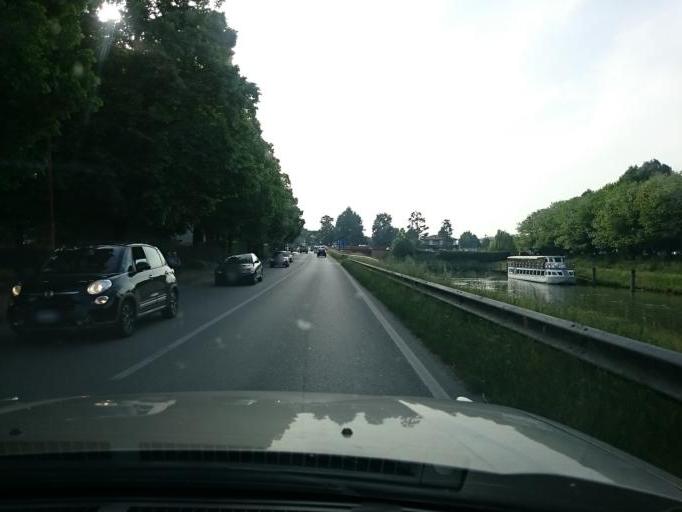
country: IT
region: Veneto
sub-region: Provincia di Venezia
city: Stra
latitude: 45.4077
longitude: 12.0078
